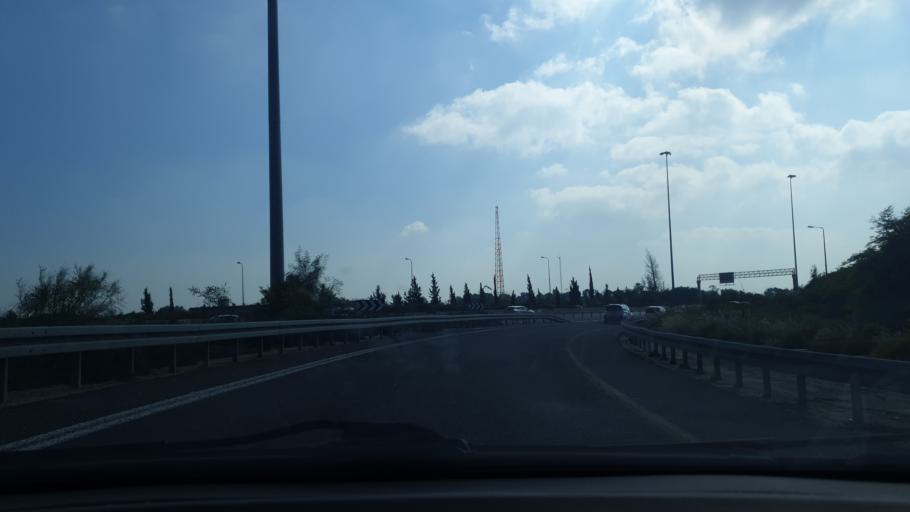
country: IL
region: Central District
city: Bet Dagan
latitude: 32.0093
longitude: 34.8131
